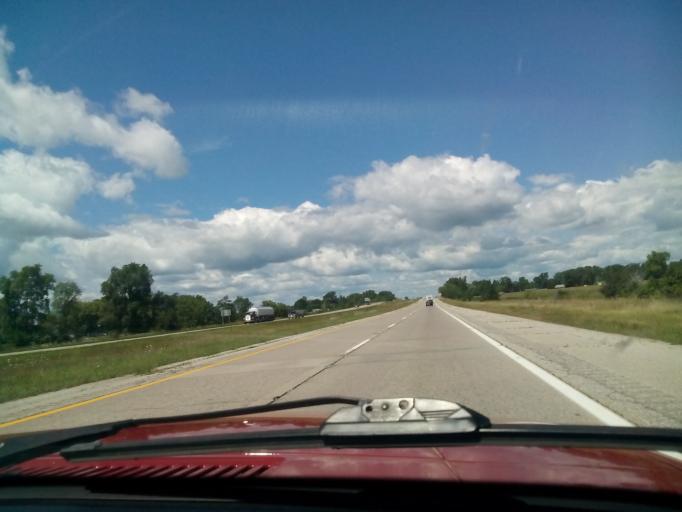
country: US
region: Michigan
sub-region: Bay County
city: Bay City
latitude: 43.6340
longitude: -83.9669
